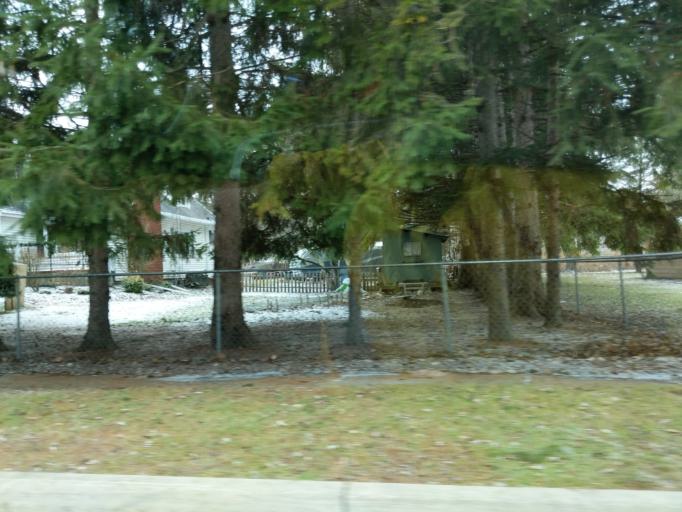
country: US
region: Michigan
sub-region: Sanilac County
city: Marlette
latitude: 43.3307
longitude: -83.0814
